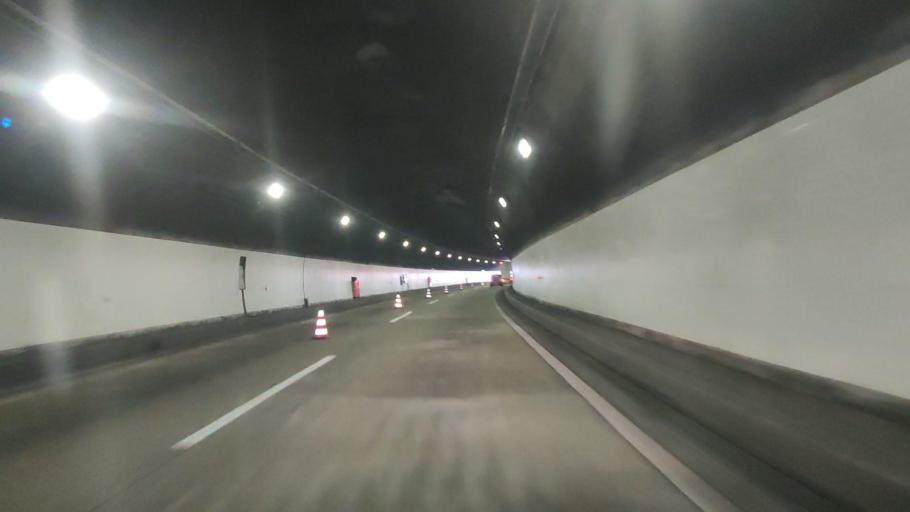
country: JP
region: Saga Prefecture
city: Takeocho-takeo
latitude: 33.1993
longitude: 130.0627
